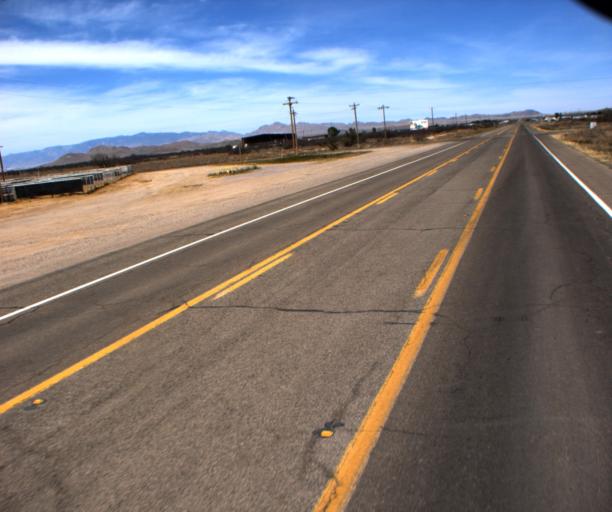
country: US
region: Arizona
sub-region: Cochise County
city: Willcox
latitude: 32.2668
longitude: -109.8226
